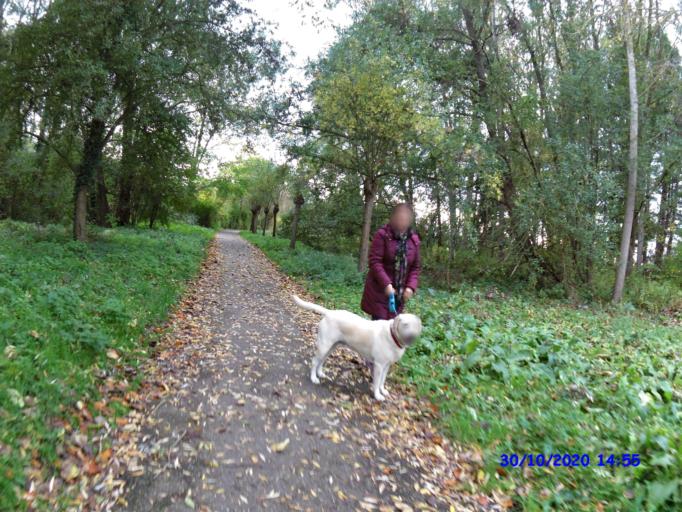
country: BE
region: Flanders
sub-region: Provincie Vlaams-Brabant
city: Landen
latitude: 50.7625
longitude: 5.0848
